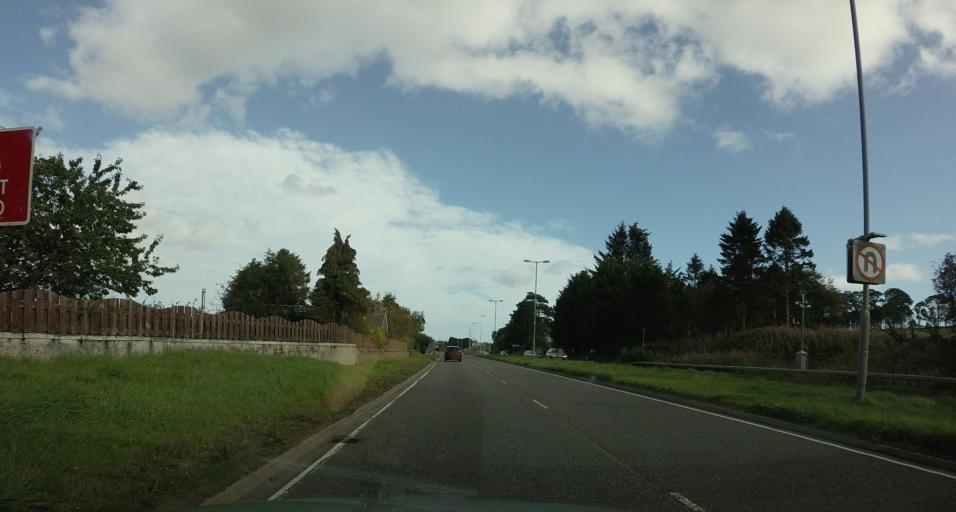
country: GB
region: Scotland
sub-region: Aberdeenshire
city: Westhill
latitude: 57.1473
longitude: -2.2610
